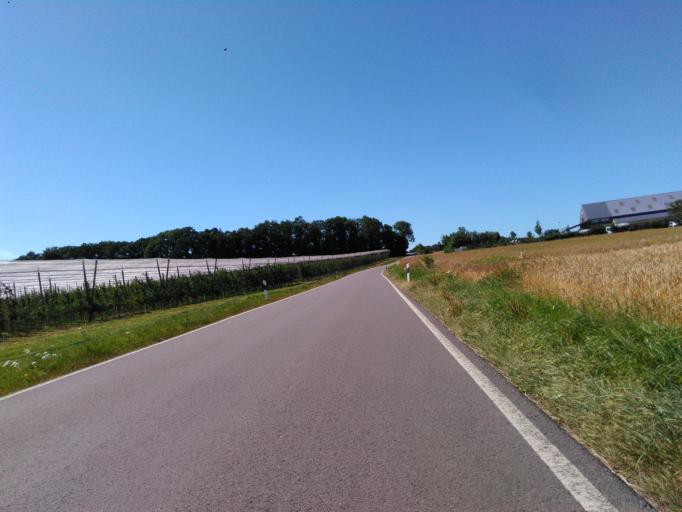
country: LU
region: Luxembourg
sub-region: Canton de Capellen
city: Dippach
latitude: 49.5637
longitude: 5.9753
